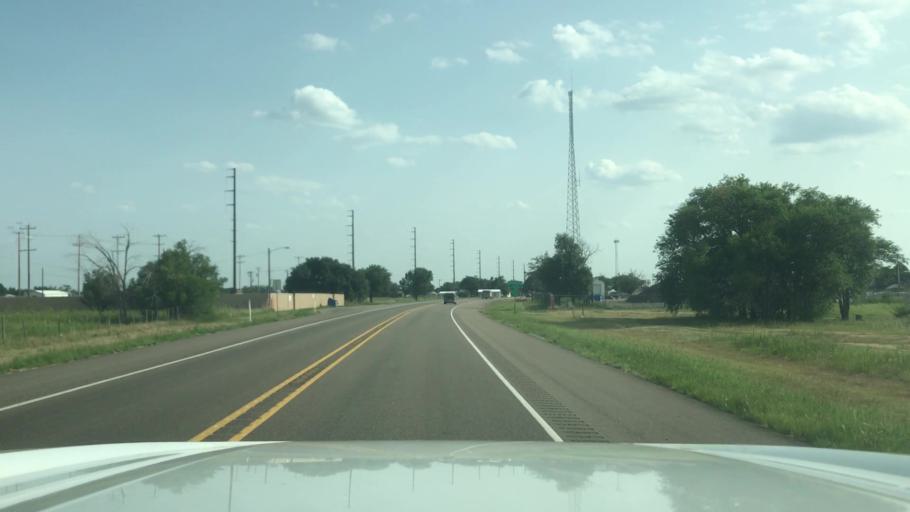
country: US
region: Texas
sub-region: Hartley County
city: Channing
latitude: 35.6903
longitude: -102.3283
